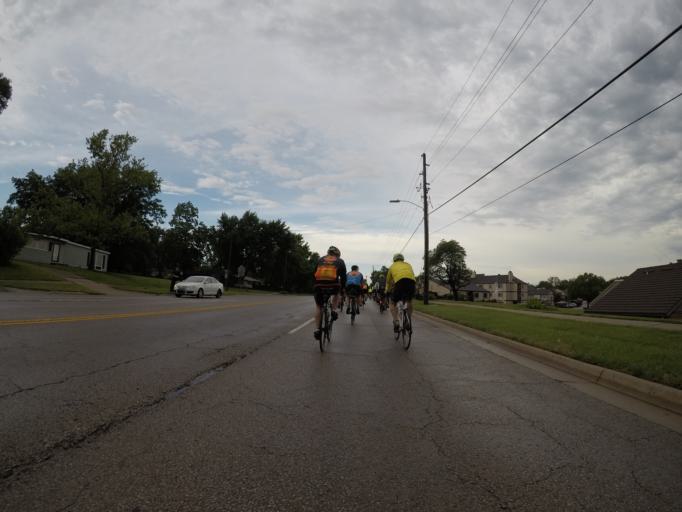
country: US
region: Kansas
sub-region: Shawnee County
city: Topeka
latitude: 39.0058
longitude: -95.7032
